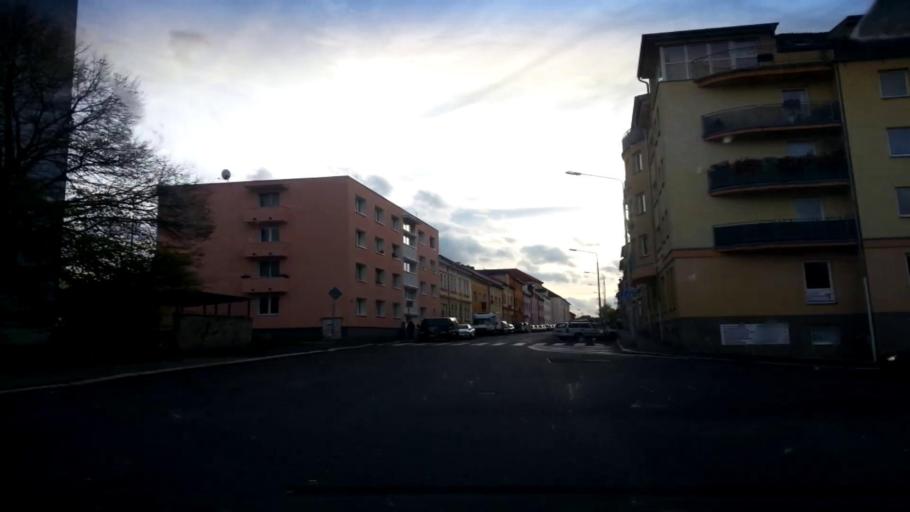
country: CZ
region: Karlovarsky
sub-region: Okres Cheb
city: Cheb
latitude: 50.0689
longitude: 12.3753
